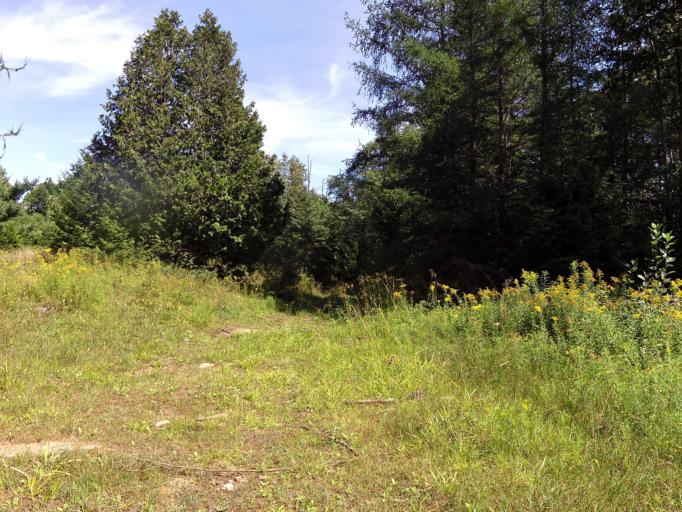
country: CA
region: Ontario
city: Renfrew
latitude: 45.0266
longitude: -76.7042
